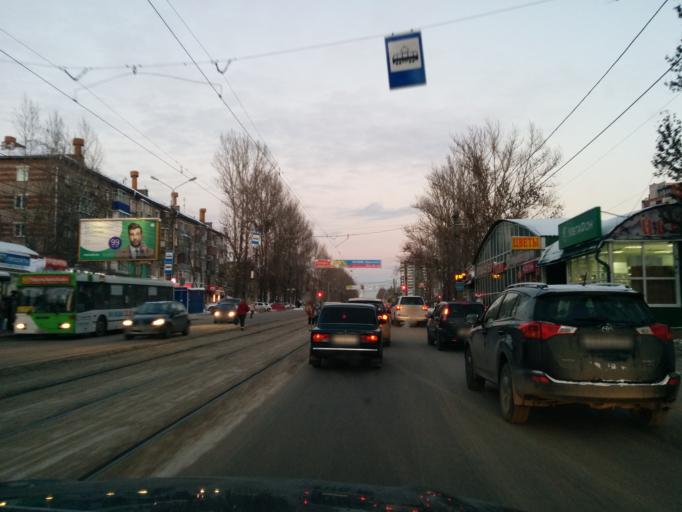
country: RU
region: Perm
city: Perm
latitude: 57.9797
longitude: 56.1911
